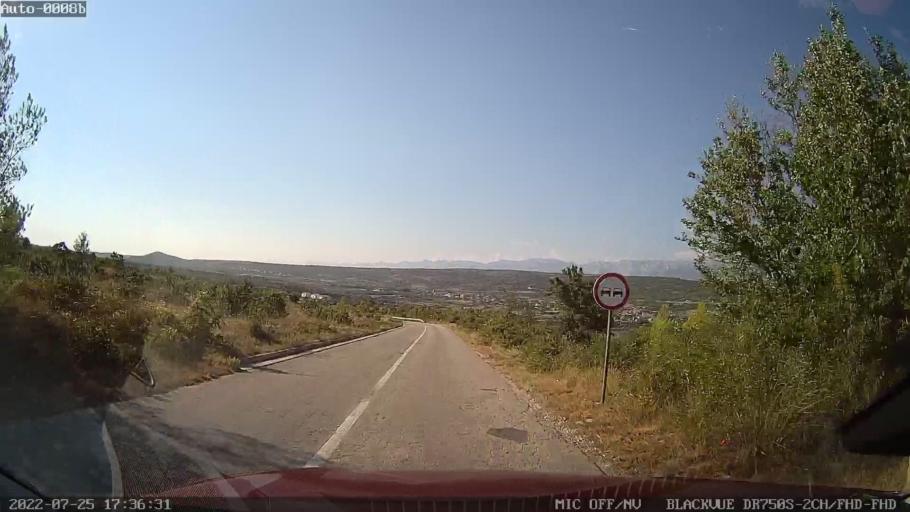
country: HR
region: Zadarska
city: Posedarje
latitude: 44.2012
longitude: 15.4710
